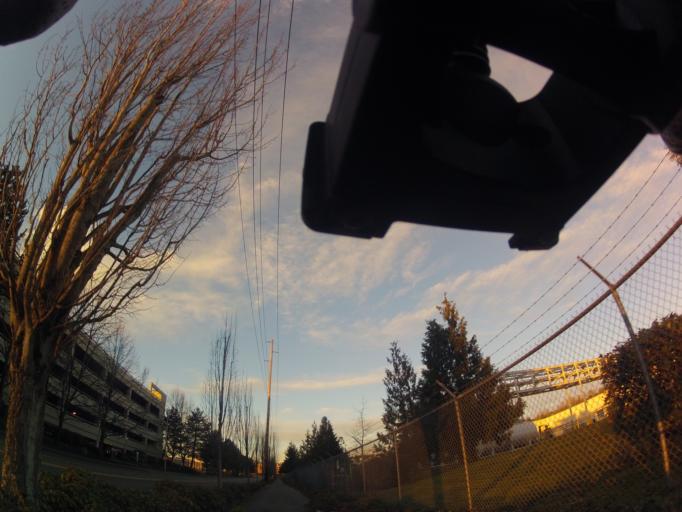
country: US
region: Washington
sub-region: King County
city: Renton
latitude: 47.4922
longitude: -122.2003
